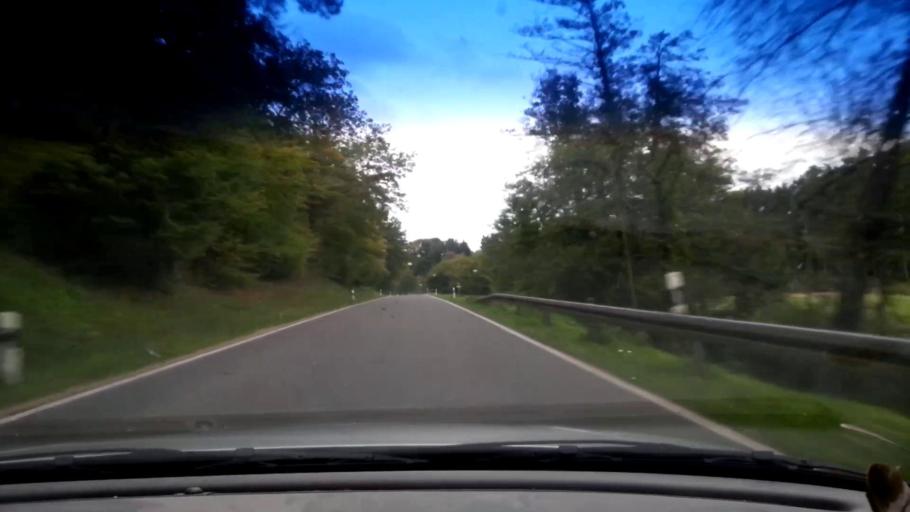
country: DE
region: Bavaria
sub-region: Upper Franconia
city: Lauter
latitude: 49.9786
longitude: 10.7748
